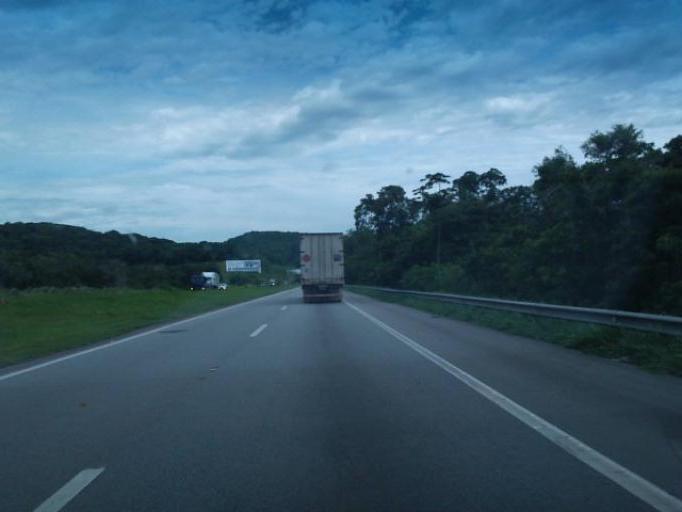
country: BR
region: Sao Paulo
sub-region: Miracatu
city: Miracatu
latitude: -24.2129
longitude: -47.3695
